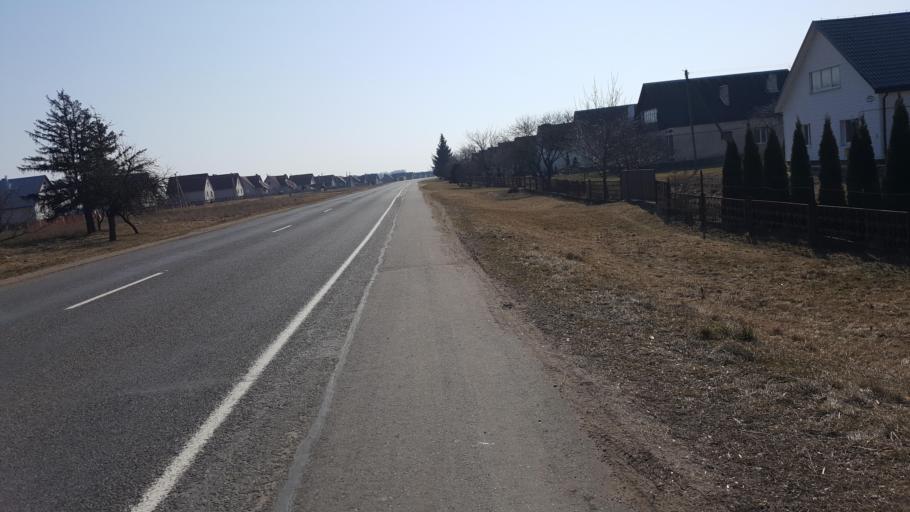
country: BY
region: Brest
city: Kamyanyets
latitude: 52.3297
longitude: 23.9150
